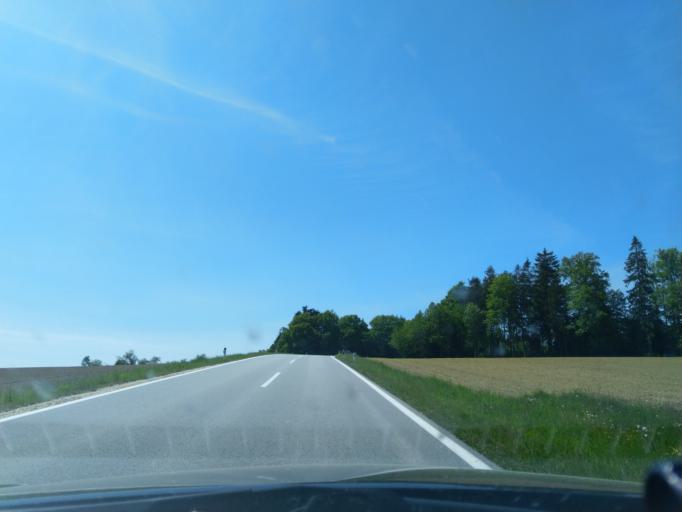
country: AT
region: Upper Austria
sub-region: Politischer Bezirk Ried im Innkreis
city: Ried im Innkreis
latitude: 48.2707
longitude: 13.4027
